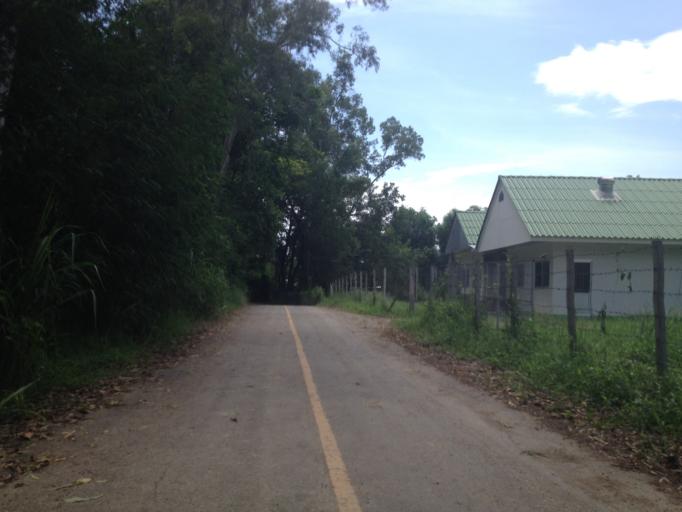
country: TH
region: Chiang Mai
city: Chiang Mai
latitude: 18.7559
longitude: 98.9255
